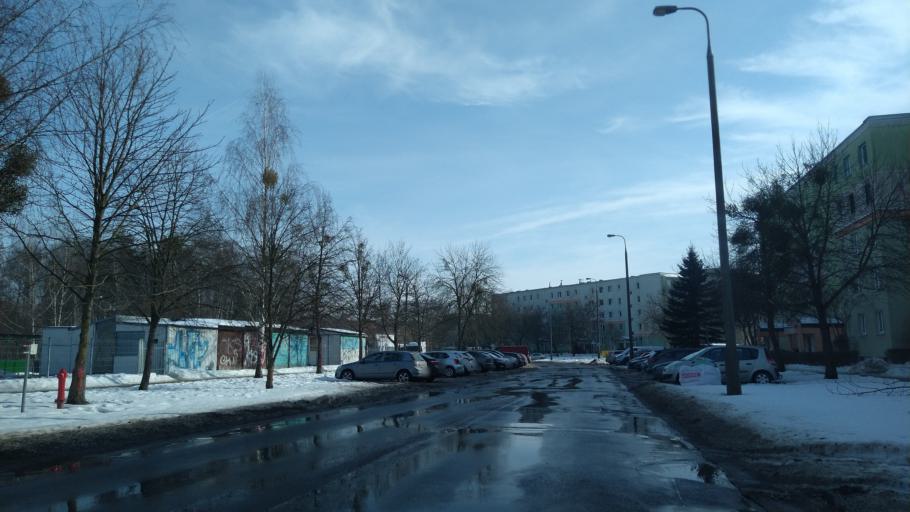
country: PL
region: Warmian-Masurian Voivodeship
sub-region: Powiat olsztynski
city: Olsztyn
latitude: 53.7409
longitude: 20.5150
